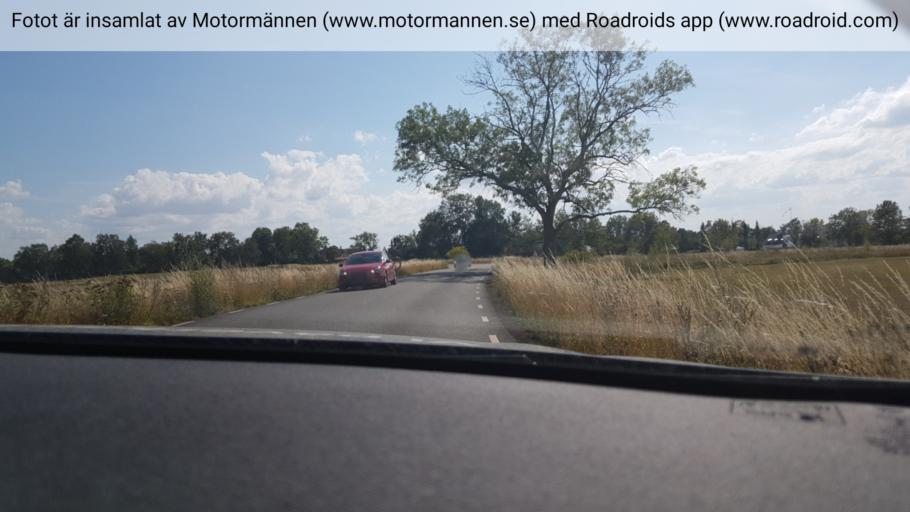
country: SE
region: Vaestra Goetaland
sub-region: Gotene Kommun
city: Kallby
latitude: 58.5383
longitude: 13.3240
